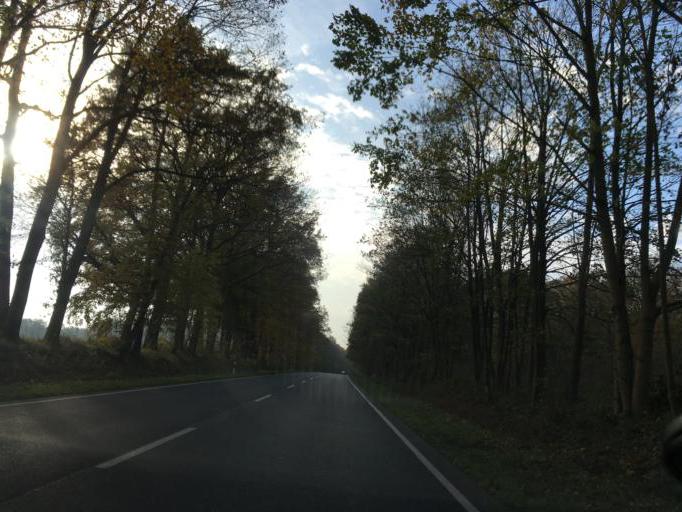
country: DE
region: Lower Saxony
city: Betzendorf
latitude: 53.1420
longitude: 10.2675
